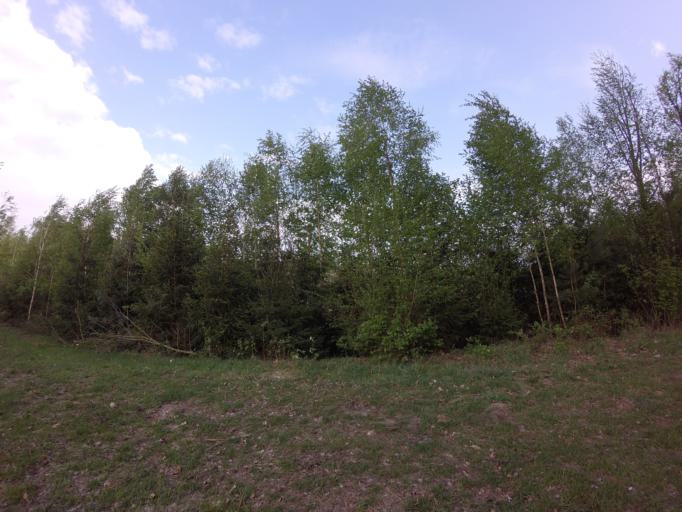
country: PL
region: West Pomeranian Voivodeship
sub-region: Powiat choszczenski
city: Choszczno
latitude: 53.1542
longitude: 15.3178
